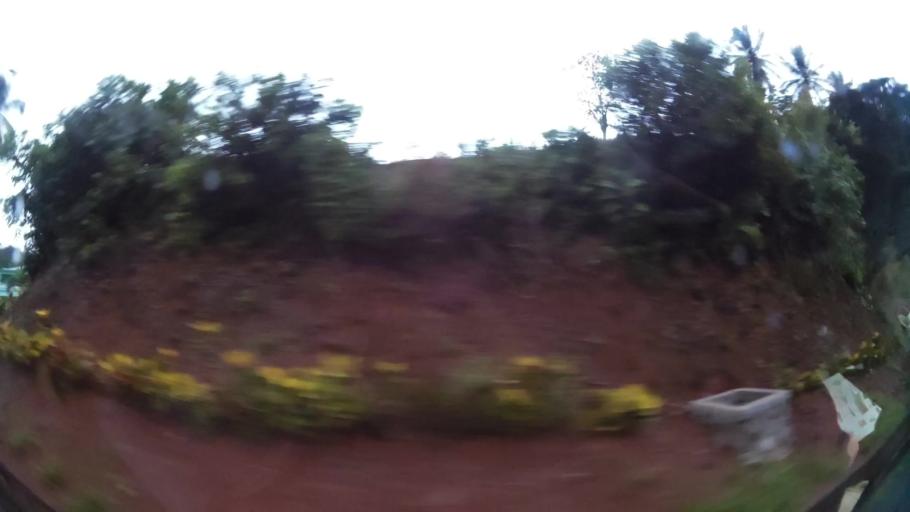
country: DM
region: Saint Andrew
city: Wesley
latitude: 15.5573
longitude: -61.3083
